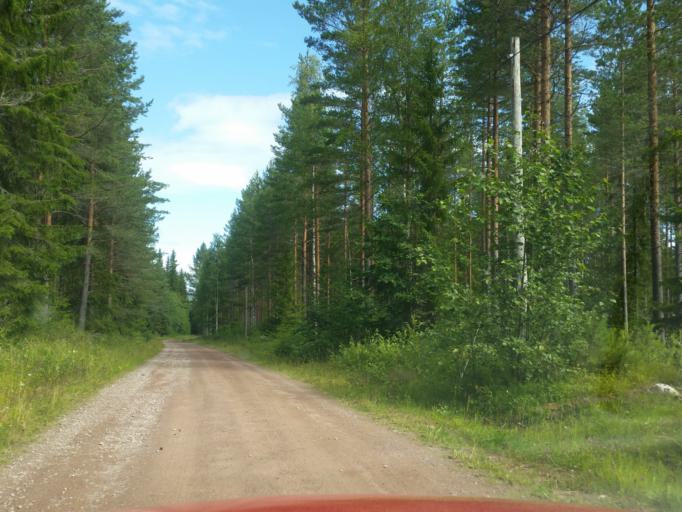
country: SE
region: Dalarna
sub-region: Gagnefs Kommun
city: Gagnef
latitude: 60.6455
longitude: 15.1622
